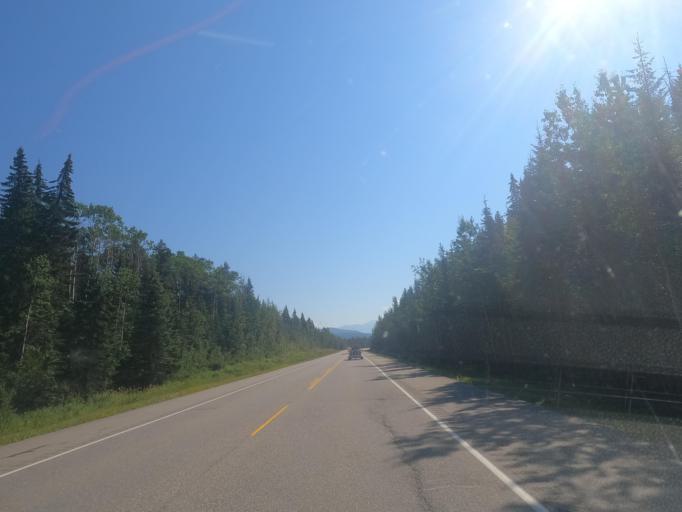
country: CA
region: Alberta
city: Jasper Park Lodge
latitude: 52.8763
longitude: -118.3223
